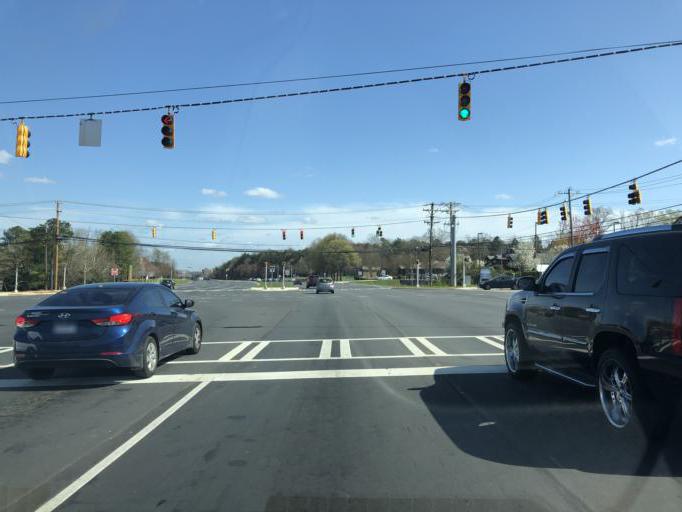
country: US
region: North Carolina
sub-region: Mecklenburg County
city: Huntersville
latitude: 35.3188
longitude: -80.7794
